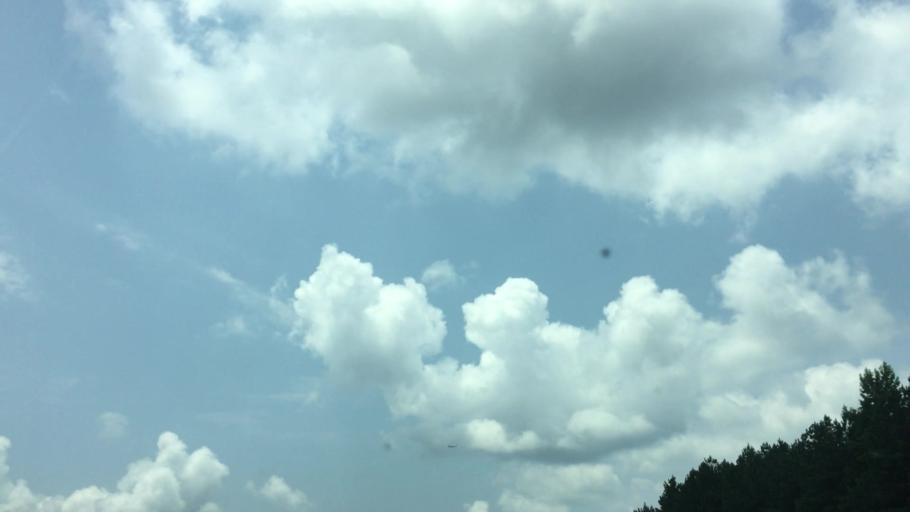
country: US
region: Georgia
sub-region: Fulton County
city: Palmetto
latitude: 33.5696
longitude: -84.6966
